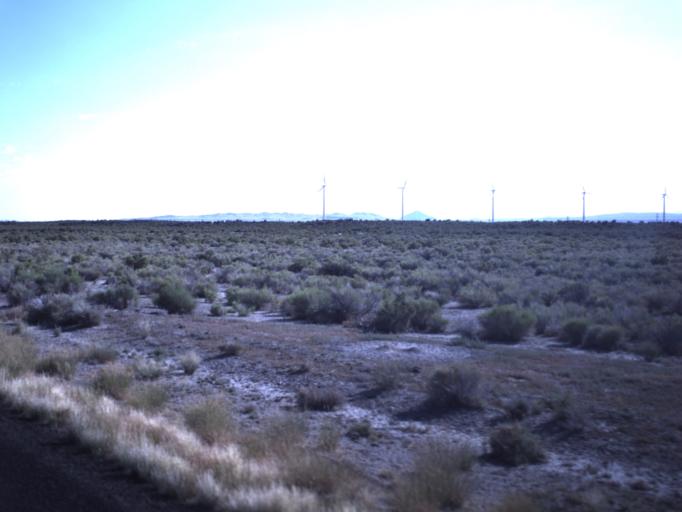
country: US
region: Utah
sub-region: Beaver County
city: Milford
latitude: 38.5804
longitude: -112.9891
